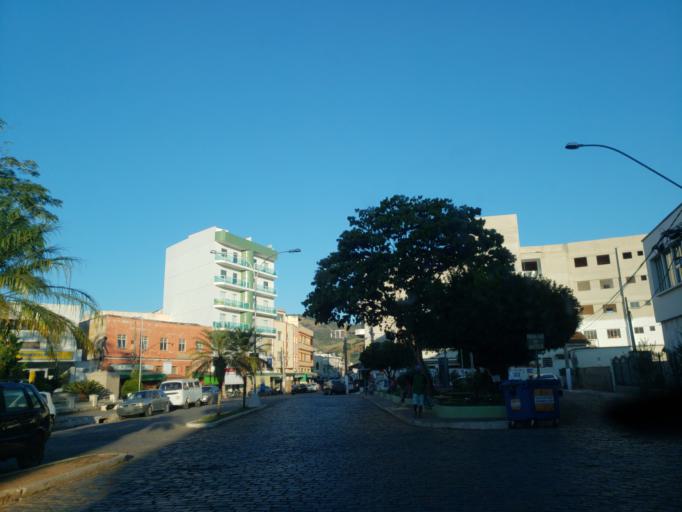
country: BR
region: Minas Gerais
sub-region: Sao Joao Nepomuceno
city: Sao Joao Nepomuceno
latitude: -21.5358
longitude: -43.0143
